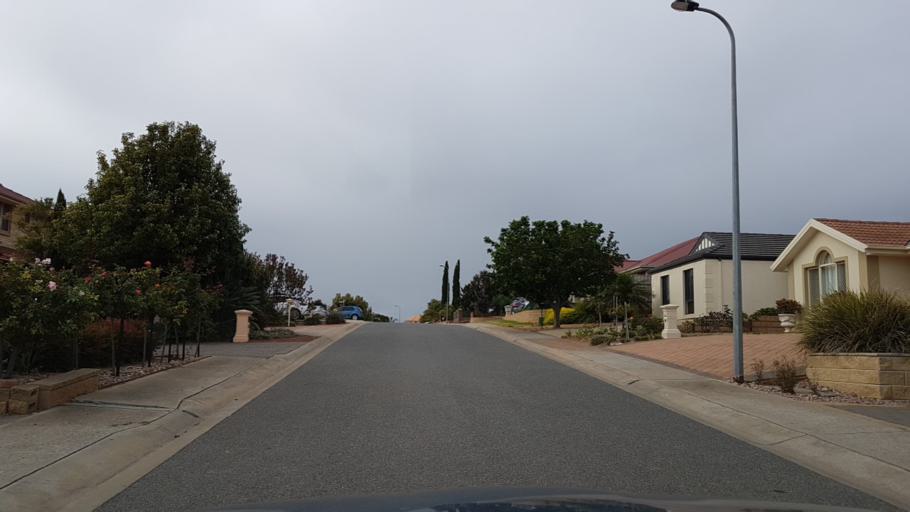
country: AU
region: South Australia
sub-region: Onkaparinga
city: Moana
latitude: -35.2089
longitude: 138.4893
